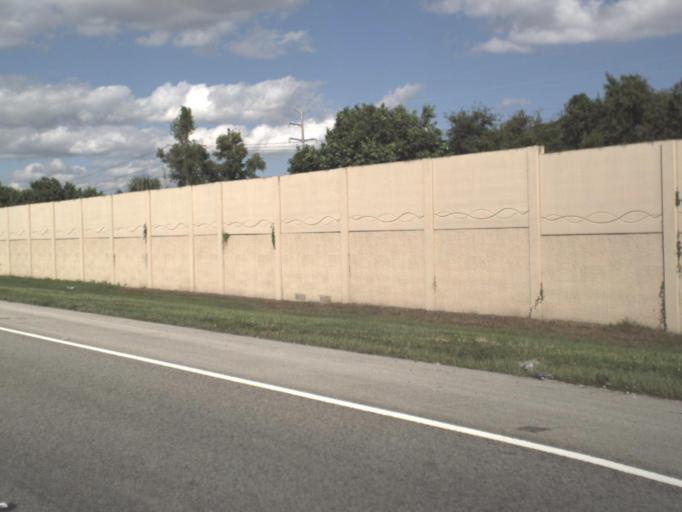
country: US
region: Florida
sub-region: Broward County
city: Lauderhill
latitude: 26.1433
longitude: -80.2192
